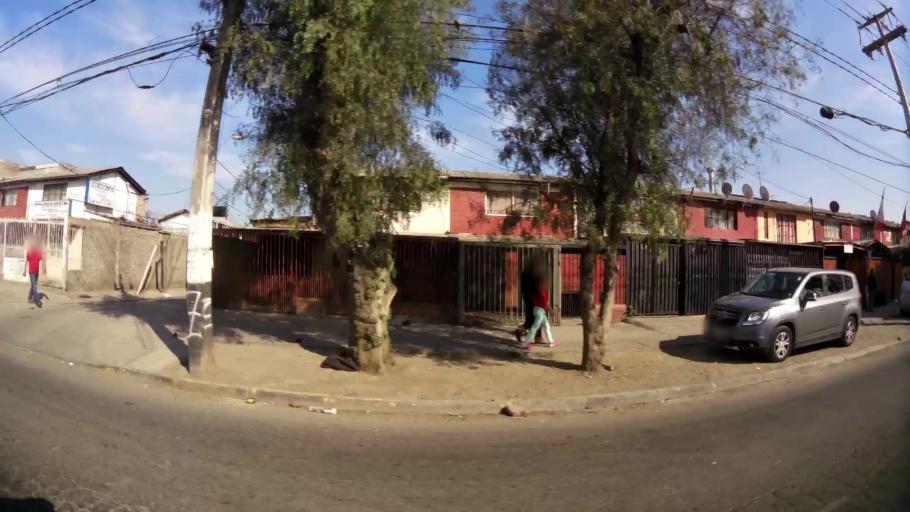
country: CL
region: Santiago Metropolitan
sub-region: Provincia de Santiago
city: Lo Prado
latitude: -33.4610
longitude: -70.7525
